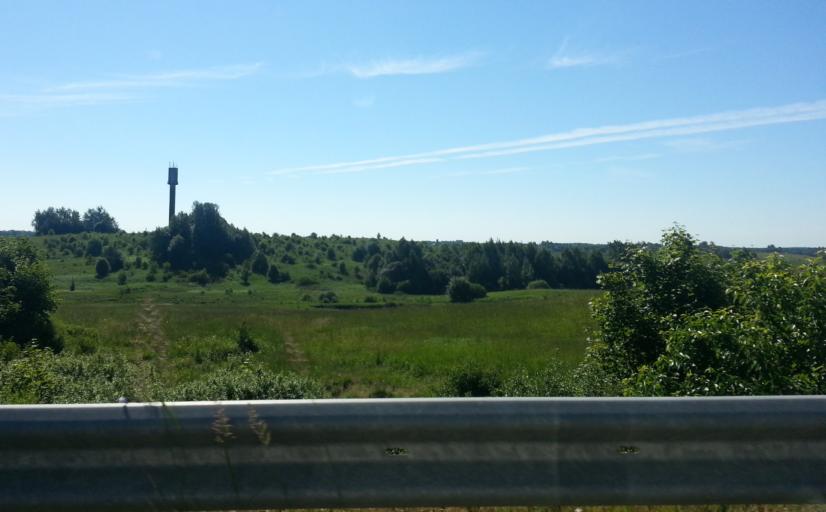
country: LT
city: Grigiskes
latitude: 54.7770
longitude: 25.0830
